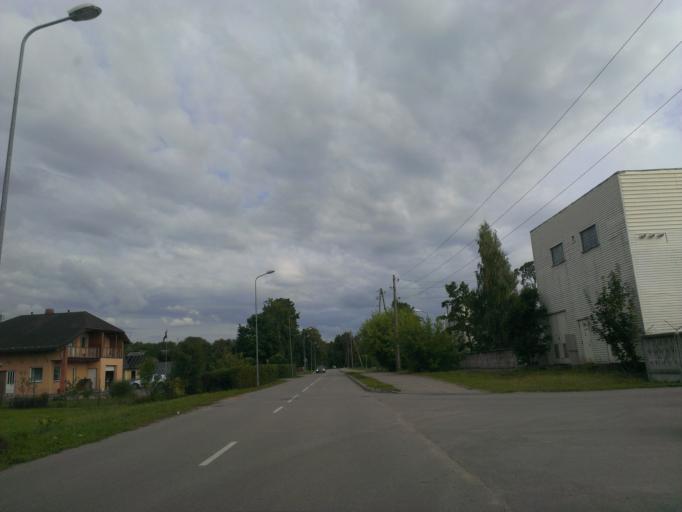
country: LV
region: Ikskile
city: Ikskile
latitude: 56.8325
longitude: 24.4833
